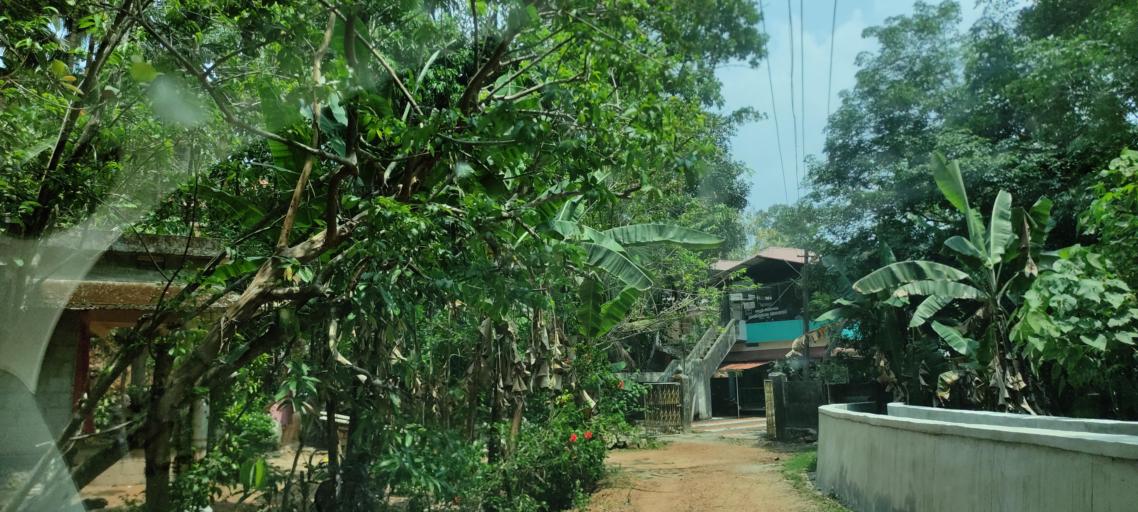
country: IN
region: Kerala
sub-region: Pattanamtitta
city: Adur
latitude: 9.1732
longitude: 76.7433
